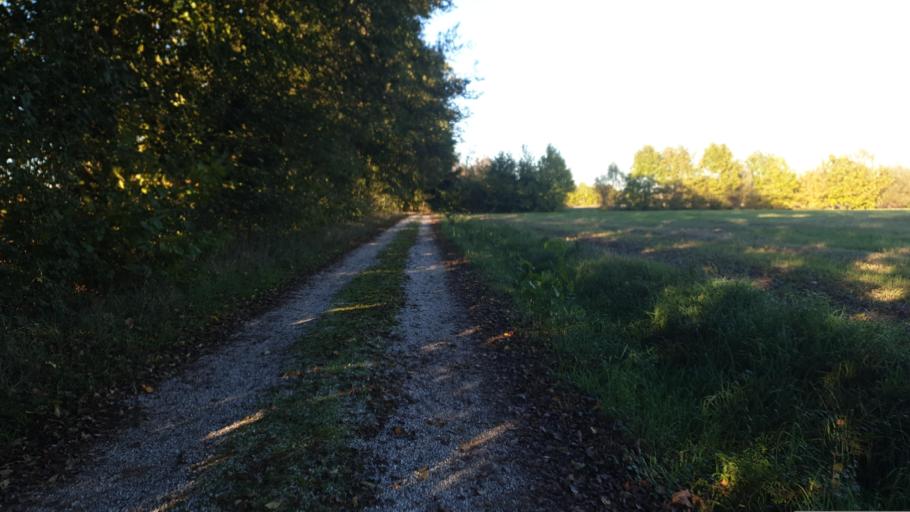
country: IT
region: Veneto
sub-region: Provincia di Venezia
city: Ballo
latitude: 45.4568
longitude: 12.0821
